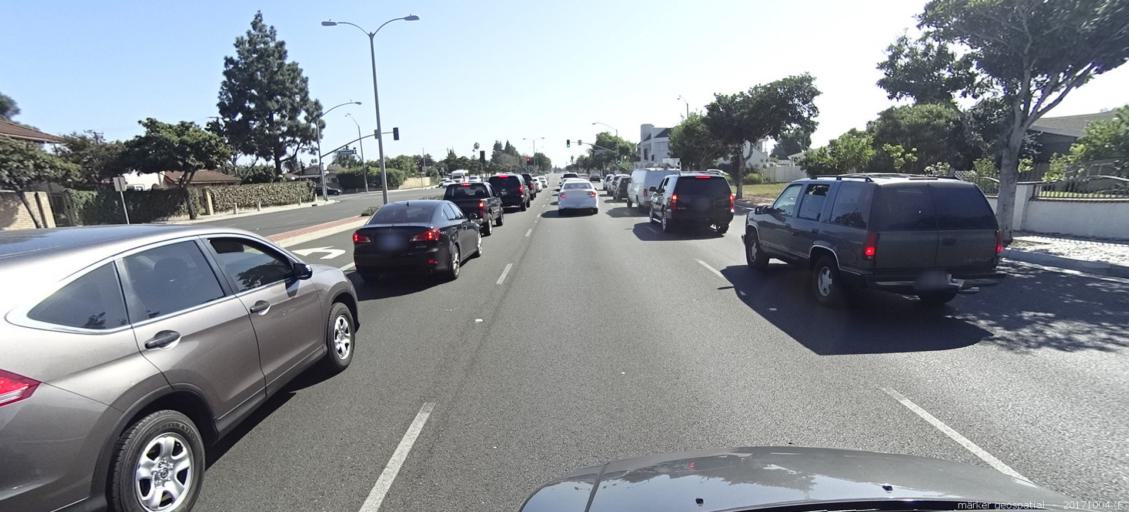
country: US
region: California
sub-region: Orange County
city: Garden Grove
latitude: 33.7967
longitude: -117.9588
